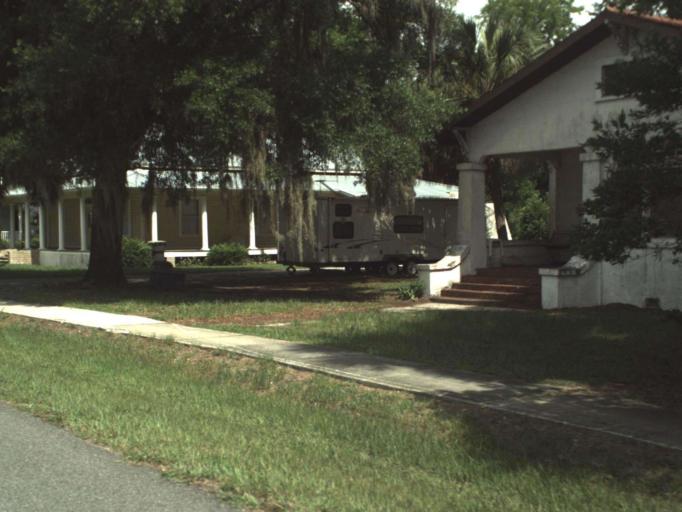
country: US
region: Florida
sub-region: Sumter County
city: Bushnell
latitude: 28.6649
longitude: -82.1088
